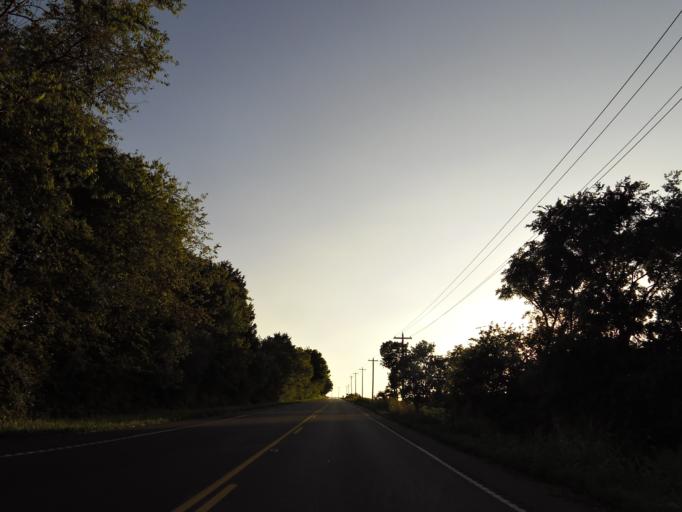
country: US
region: Tennessee
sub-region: Jefferson County
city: Dandridge
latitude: 36.0420
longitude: -83.3583
